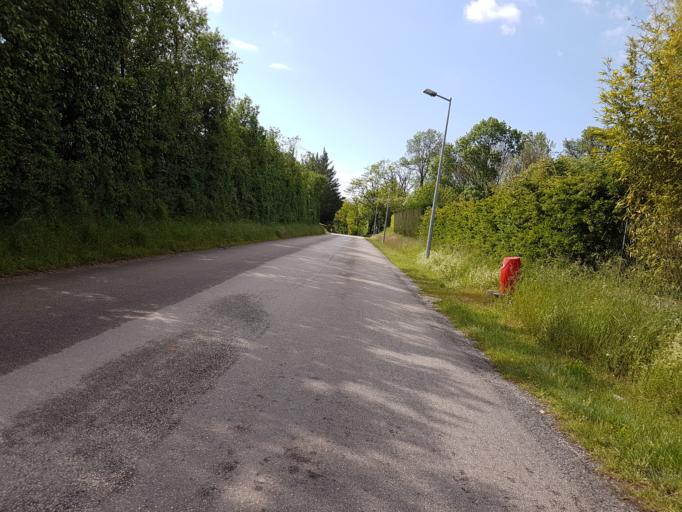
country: FR
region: Rhone-Alpes
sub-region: Departement de l'Isere
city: Bouvesse-Quirieu
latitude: 45.8106
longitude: 5.4387
